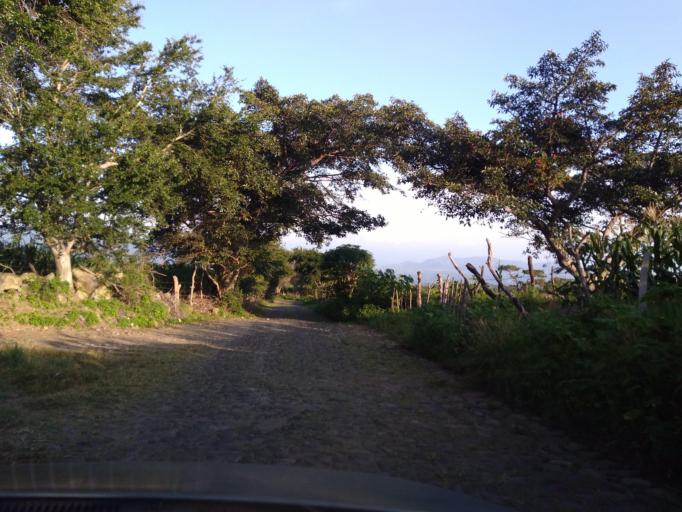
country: MX
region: Jalisco
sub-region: Tonila
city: San Marcos
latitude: 19.4592
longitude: -103.5209
